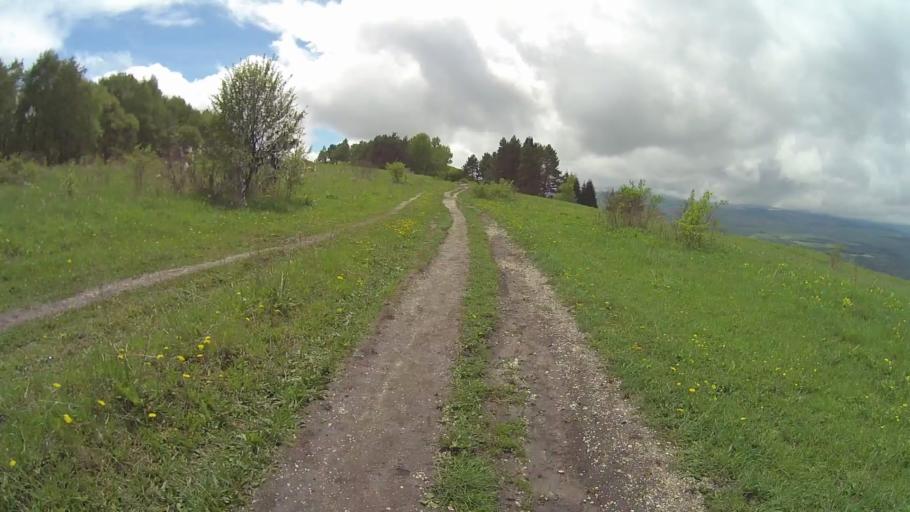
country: RU
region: Stavropol'skiy
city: Kislovodsk
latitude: 43.8883
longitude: 42.7675
